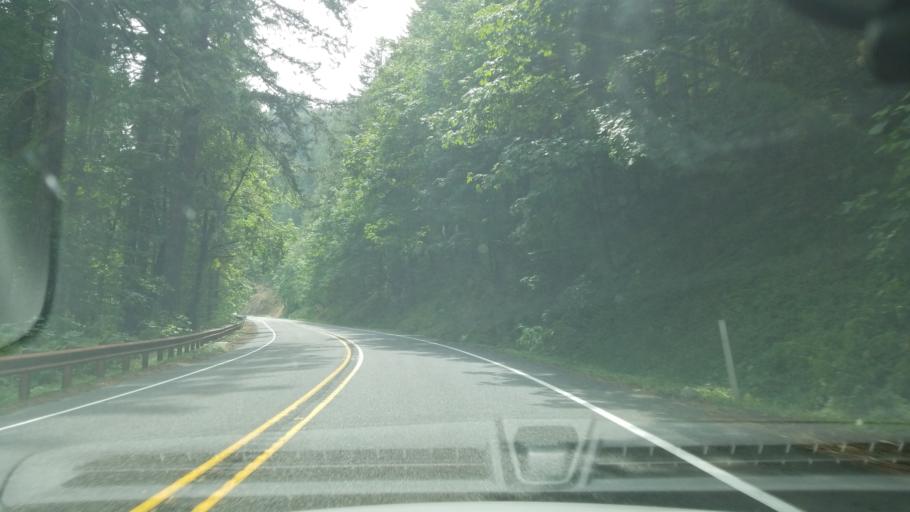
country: US
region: Washington
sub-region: Clark County
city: Washougal
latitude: 45.5849
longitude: -122.1923
